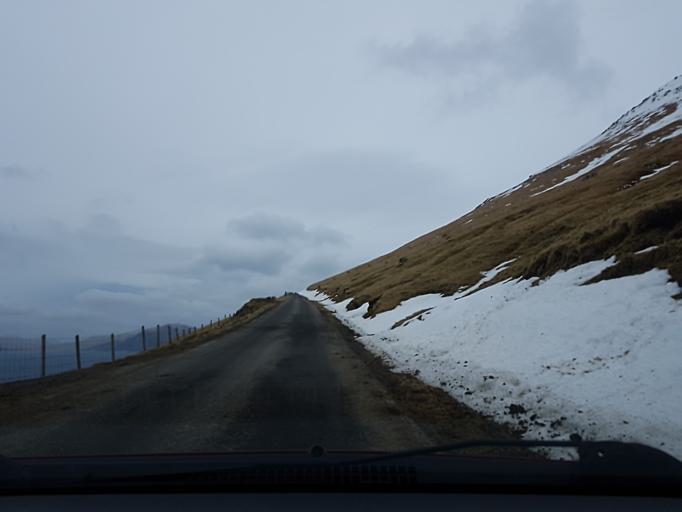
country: FO
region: Streymoy
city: Kollafjordhur
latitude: 62.0014
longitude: -6.9011
